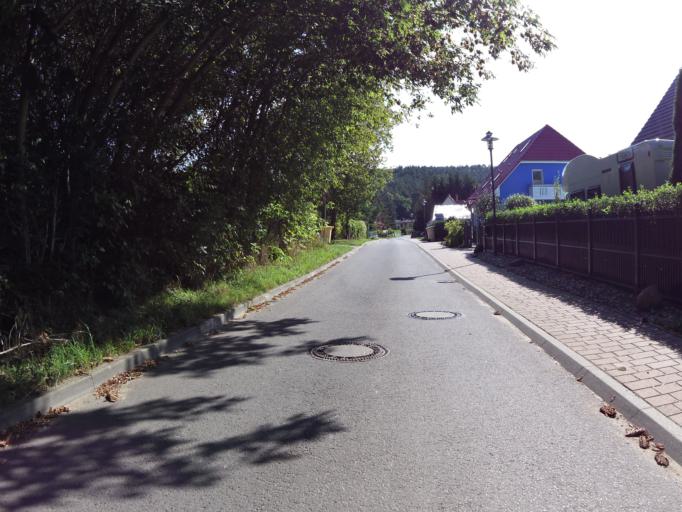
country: DE
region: Mecklenburg-Vorpommern
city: Seebad Heringsdorf
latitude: 53.9349
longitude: 14.1841
